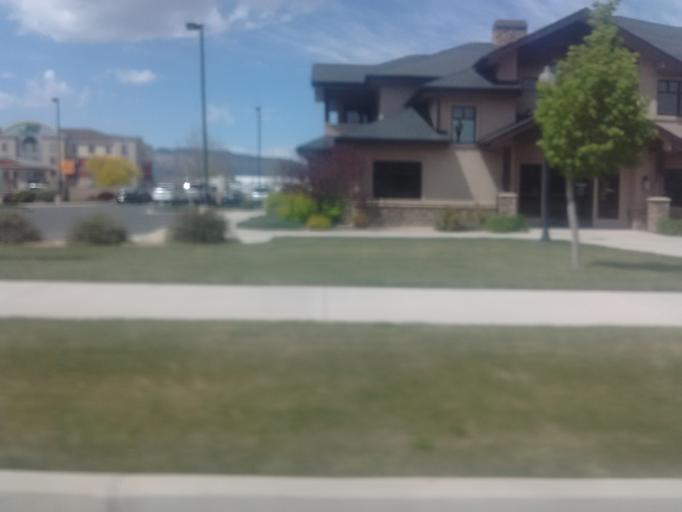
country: US
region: Colorado
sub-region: Mesa County
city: Redlands
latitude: 39.0966
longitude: -108.6083
